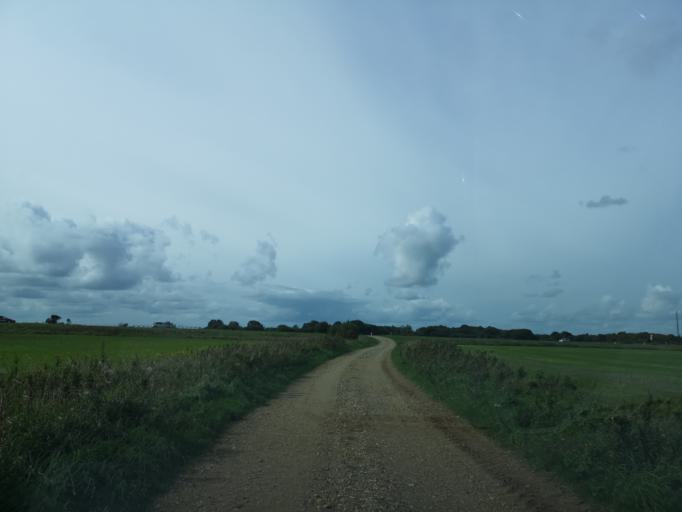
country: DK
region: Central Jutland
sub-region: Ringkobing-Skjern Kommune
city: Skjern
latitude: 55.9308
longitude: 8.5137
